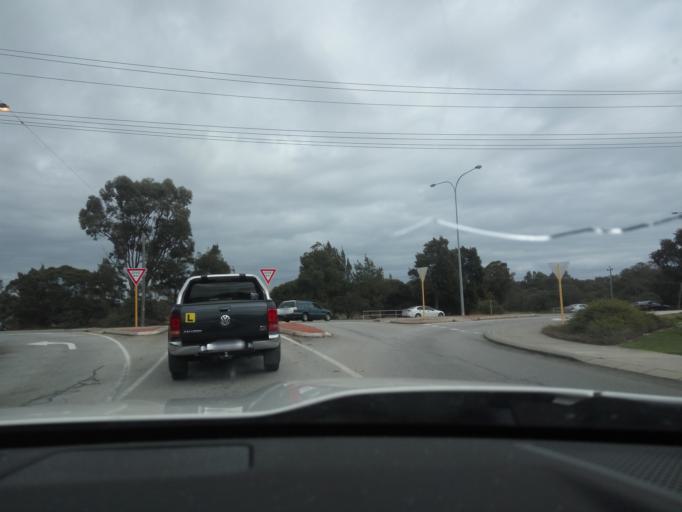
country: AU
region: Western Australia
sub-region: City of Cockburn
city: South Lake
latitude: -32.1095
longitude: 115.8307
